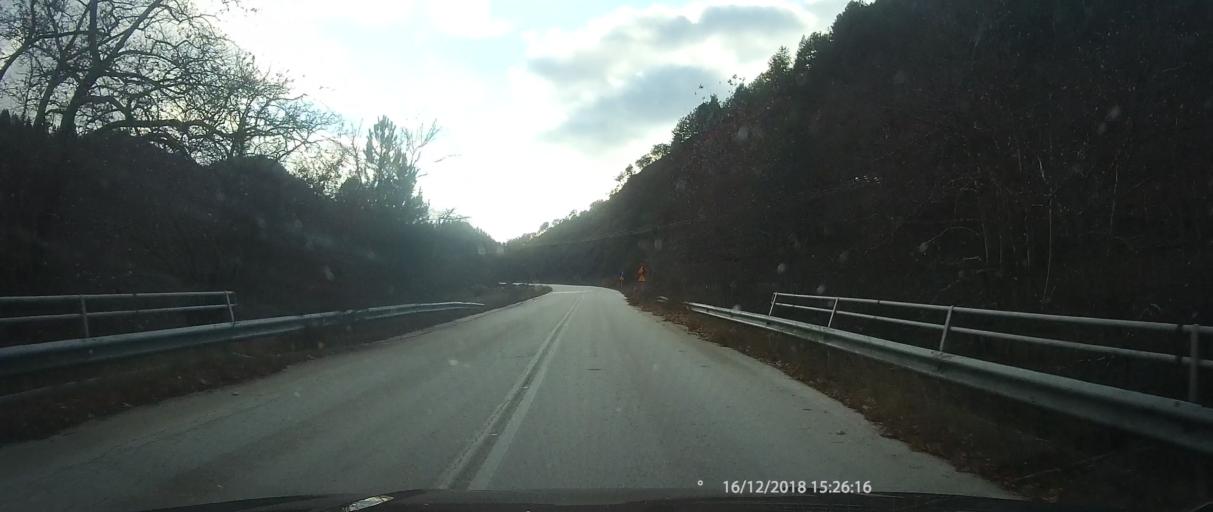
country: GR
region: Epirus
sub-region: Nomos Ioanninon
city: Konitsa
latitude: 40.1198
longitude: 20.7815
